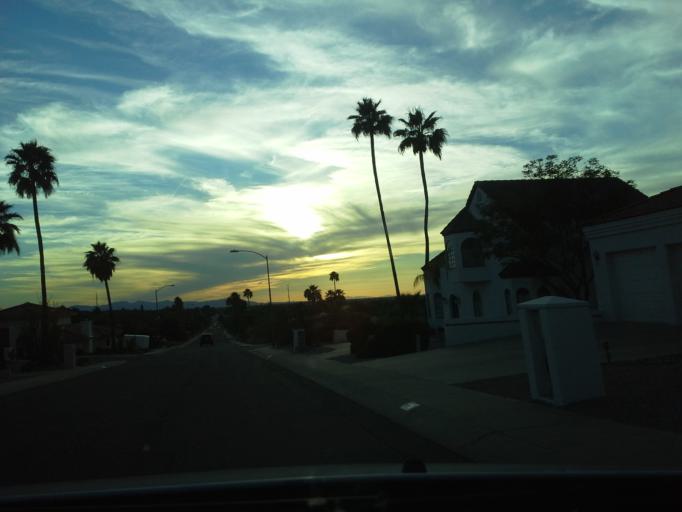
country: US
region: Arizona
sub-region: Maricopa County
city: Paradise Valley
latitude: 33.6258
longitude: -112.0598
